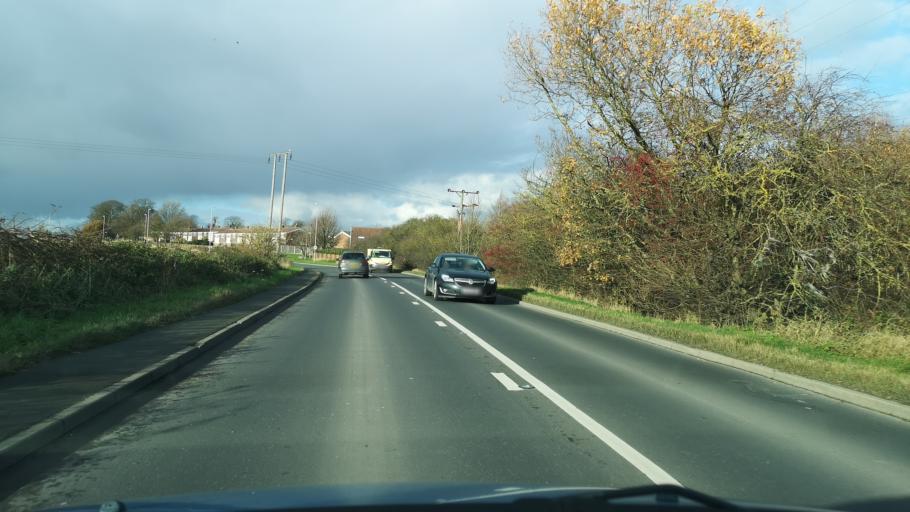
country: GB
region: England
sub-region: City and Borough of Wakefield
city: Featherstone
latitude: 53.6879
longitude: -1.3758
